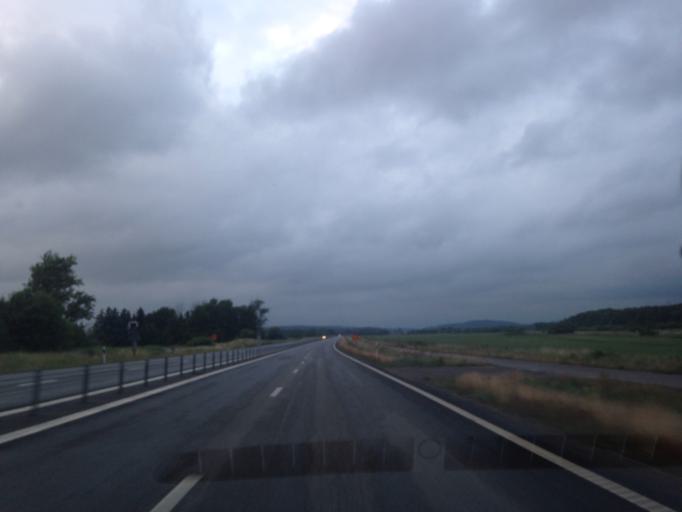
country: SE
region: Halland
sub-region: Varbergs Kommun
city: Varberg
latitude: 57.1292
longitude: 12.2615
